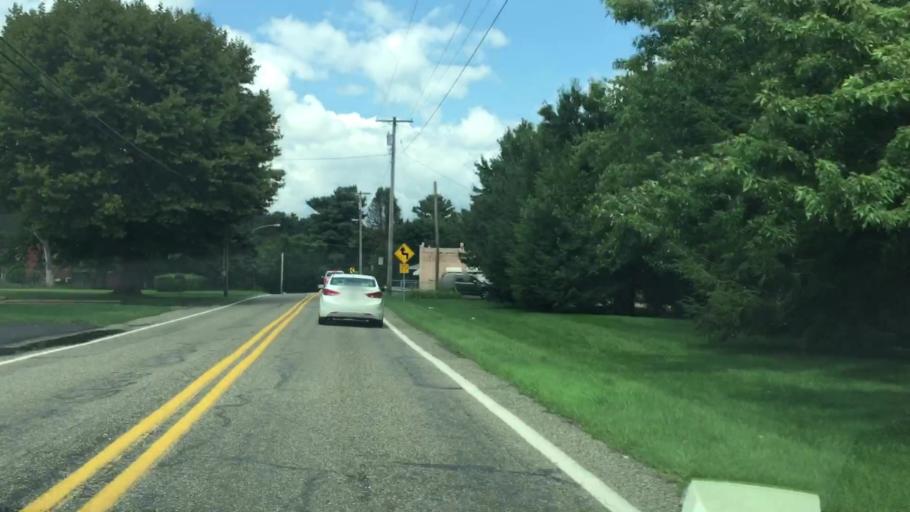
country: US
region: Pennsylvania
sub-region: Allegheny County
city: Cheswick
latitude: 40.5524
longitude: -79.8053
